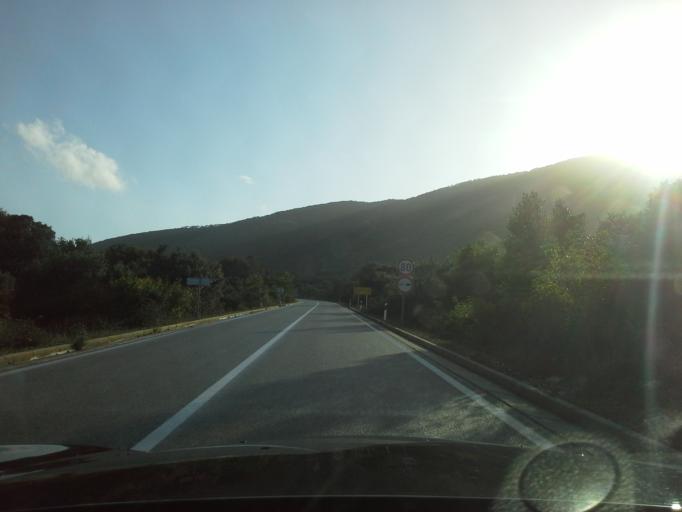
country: HR
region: Primorsko-Goranska
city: Mali Losinj
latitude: 44.6655
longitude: 14.3937
